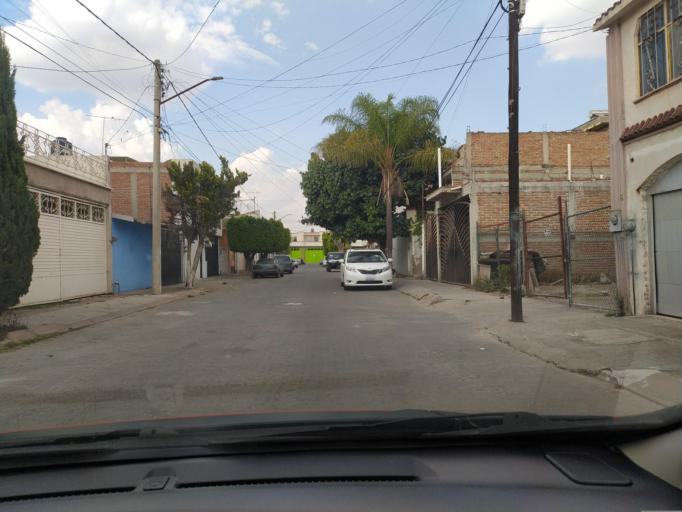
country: MX
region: Guanajuato
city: San Francisco del Rincon
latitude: 21.0234
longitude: -101.8527
